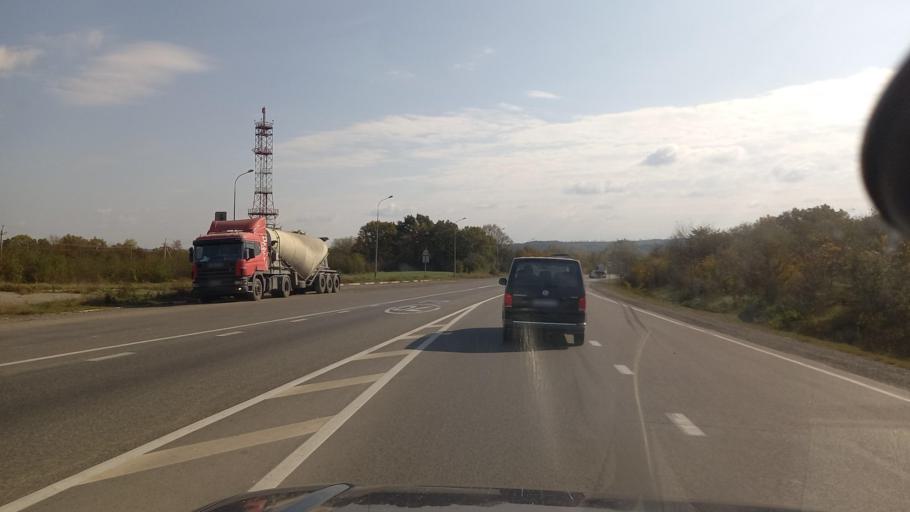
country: RU
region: Krasnodarskiy
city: Abinsk
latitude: 44.8482
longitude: 38.1448
